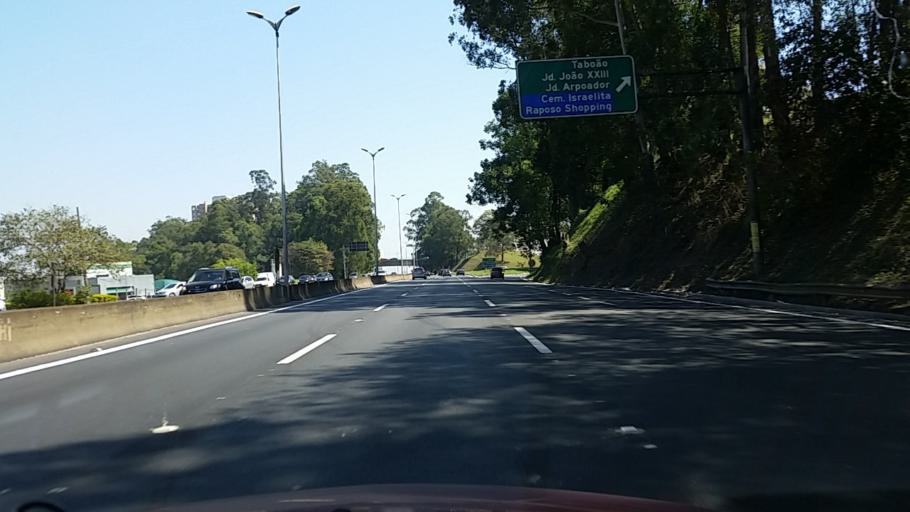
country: BR
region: Sao Paulo
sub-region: Taboao Da Serra
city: Taboao da Serra
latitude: -23.5861
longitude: -46.7594
